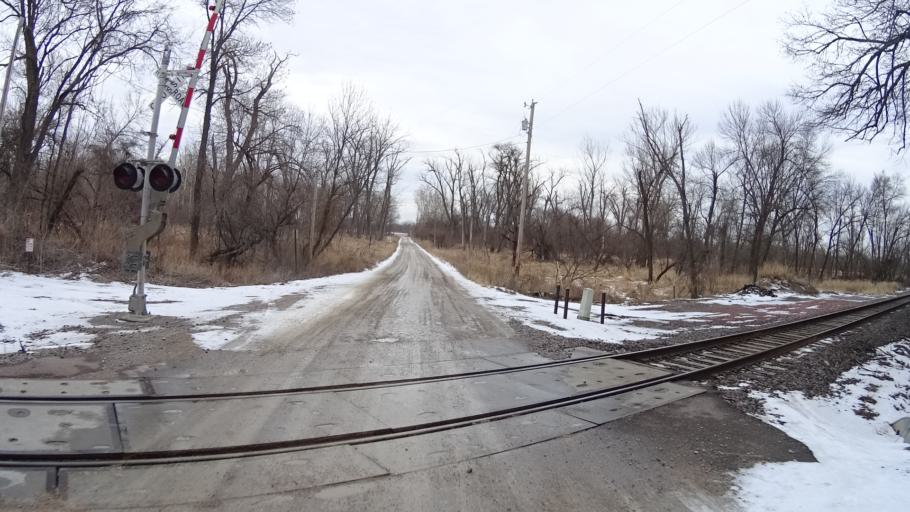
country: US
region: Nebraska
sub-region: Sarpy County
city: Bellevue
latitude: 41.1751
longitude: -95.8953
